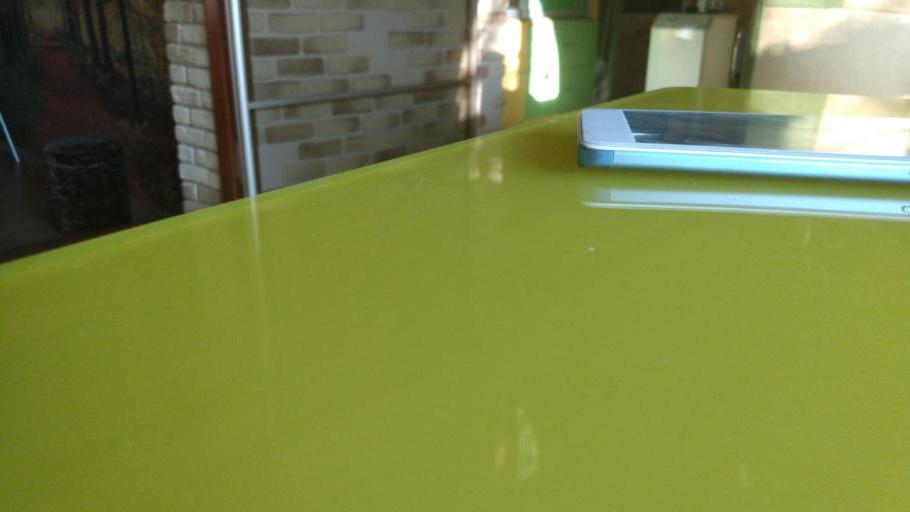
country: RU
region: Tverskaya
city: Vyshniy Volochek
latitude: 57.4506
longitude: 34.5741
